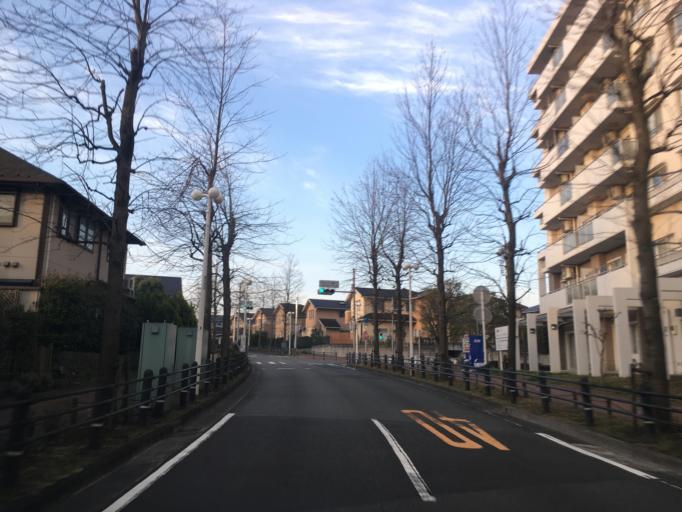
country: JP
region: Tokyo
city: Hino
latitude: 35.6156
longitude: 139.3903
